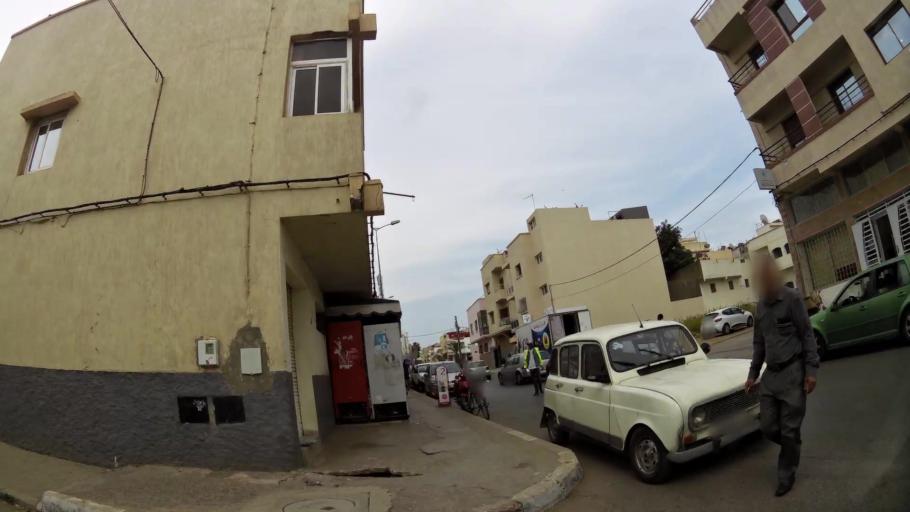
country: MA
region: Rabat-Sale-Zemmour-Zaer
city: Sale
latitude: 34.0308
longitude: -6.8091
